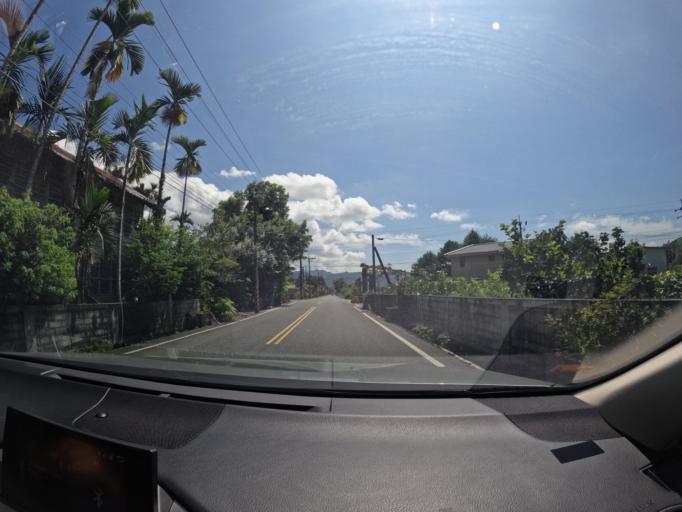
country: TW
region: Taiwan
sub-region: Hualien
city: Hualian
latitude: 23.5810
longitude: 121.3694
